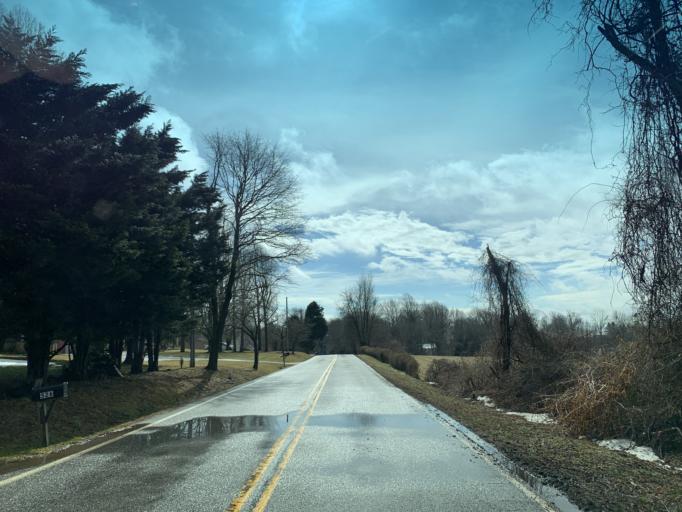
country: US
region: Delaware
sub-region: New Castle County
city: Newark
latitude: 39.7137
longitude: -75.8001
